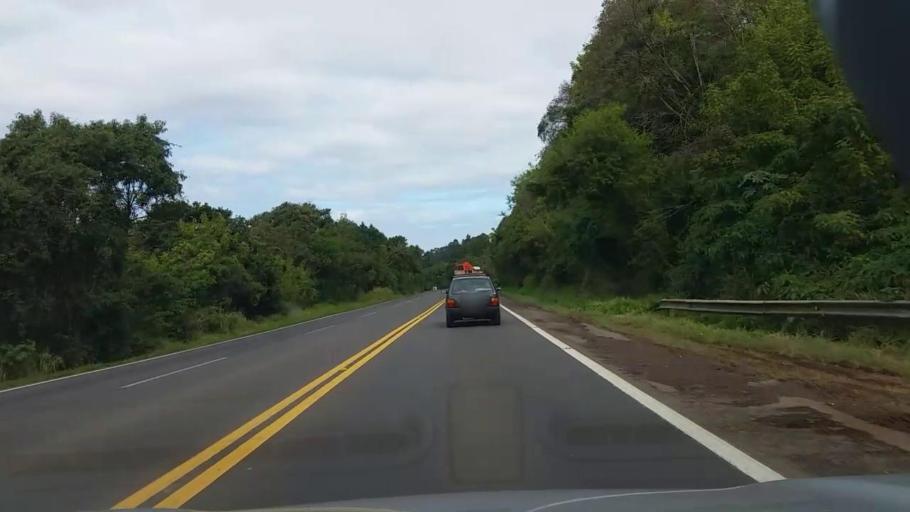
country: BR
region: Rio Grande do Sul
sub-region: Arroio Do Meio
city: Arroio do Meio
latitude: -29.3912
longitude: -52.0420
